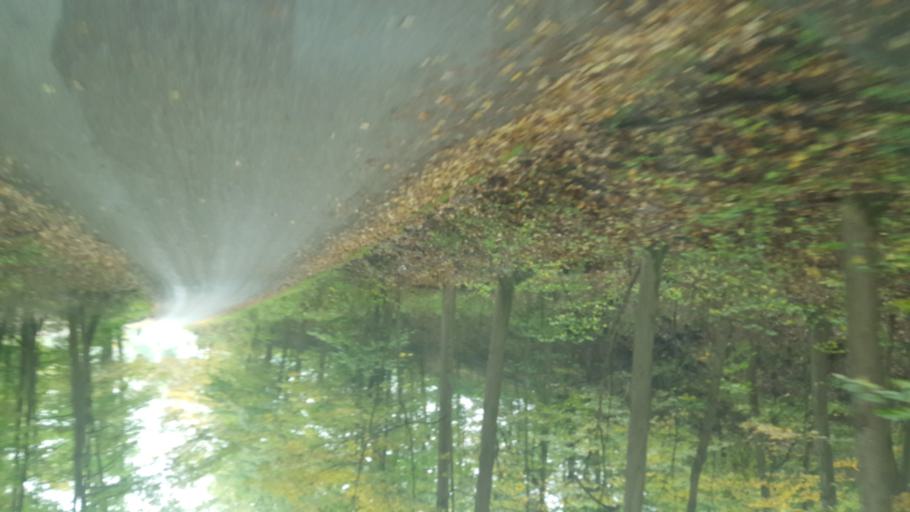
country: US
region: Ohio
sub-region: Tuscarawas County
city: Sugarcreek
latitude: 40.5586
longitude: -81.7662
